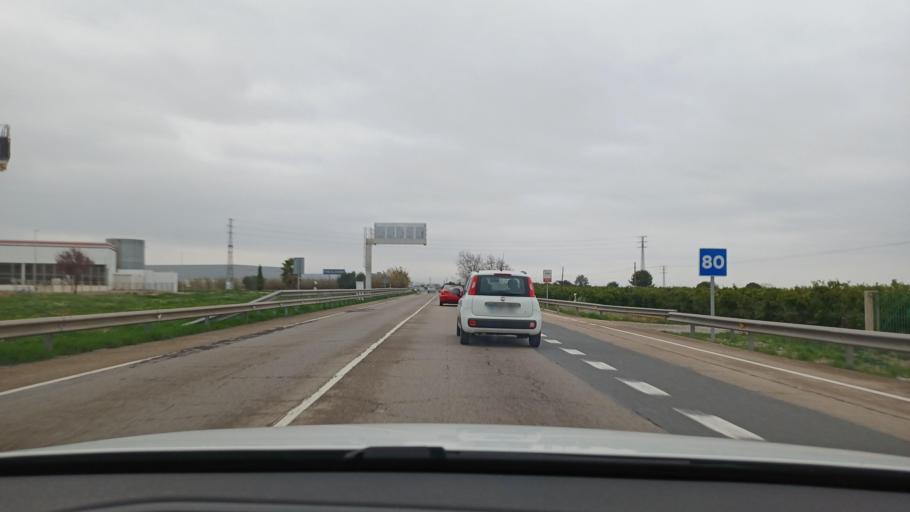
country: ES
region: Valencia
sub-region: Provincia de Castello
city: Alquerias del Nino Perdido
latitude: 39.9035
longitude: -0.1174
